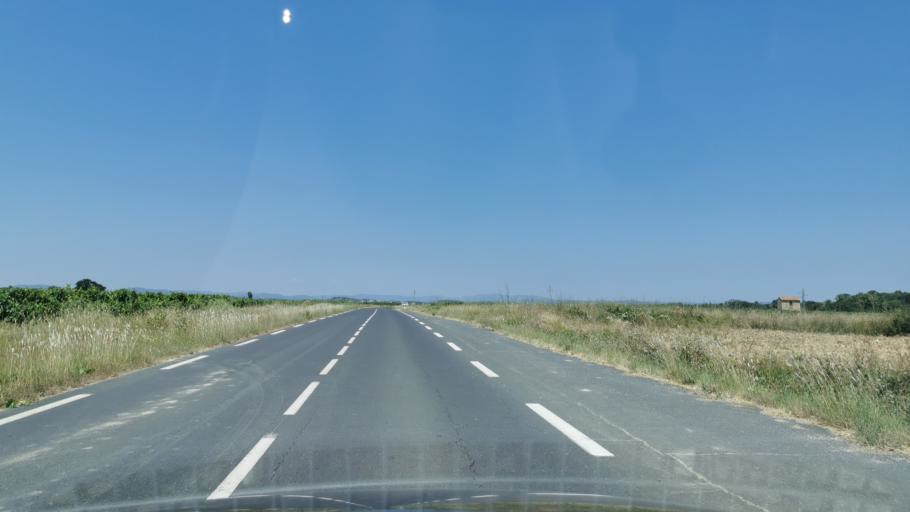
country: FR
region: Languedoc-Roussillon
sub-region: Departement de l'Herault
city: Maureilhan
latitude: 43.3660
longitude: 3.1165
